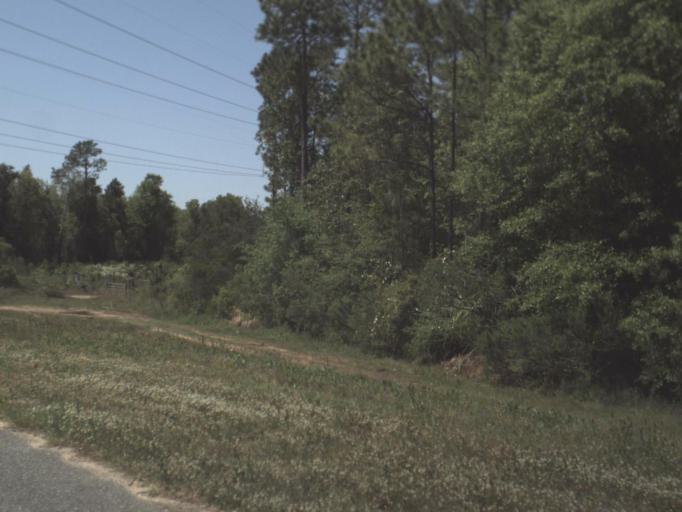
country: US
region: Florida
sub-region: Escambia County
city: Bellview
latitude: 30.4979
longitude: -87.3342
